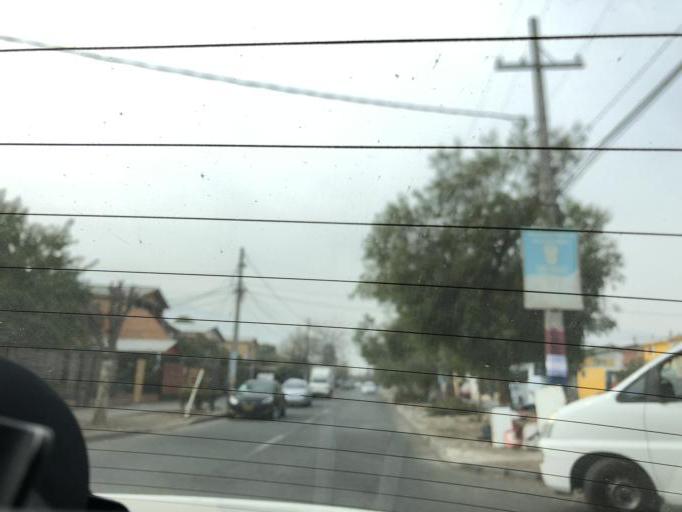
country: CL
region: Santiago Metropolitan
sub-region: Provincia de Cordillera
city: Puente Alto
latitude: -33.5935
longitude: -70.5709
